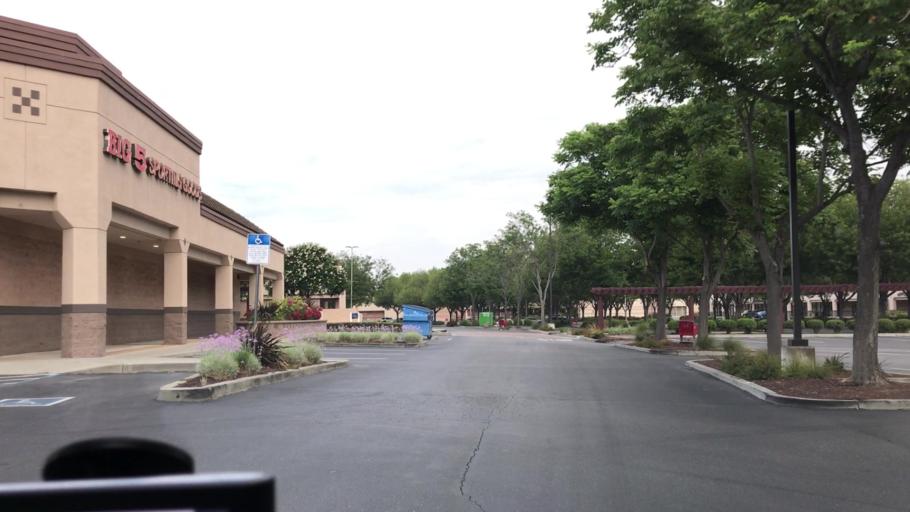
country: US
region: California
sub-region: Alameda County
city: Livermore
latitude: 37.6999
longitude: -121.7440
